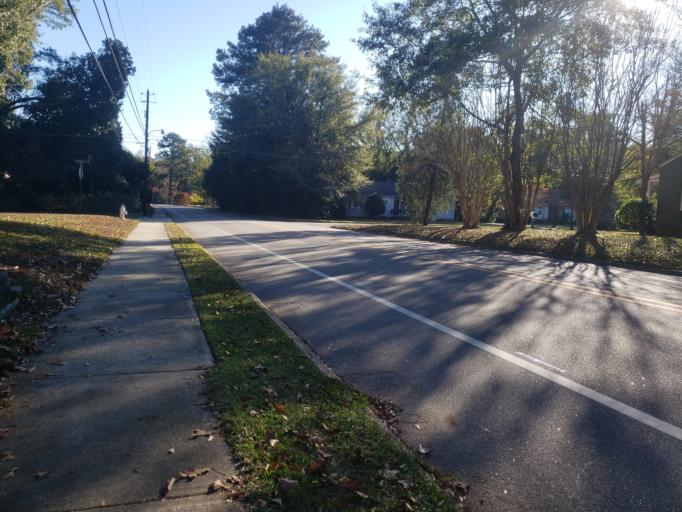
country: US
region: Alabama
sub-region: Lee County
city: Auburn
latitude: 32.5929
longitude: -85.4800
